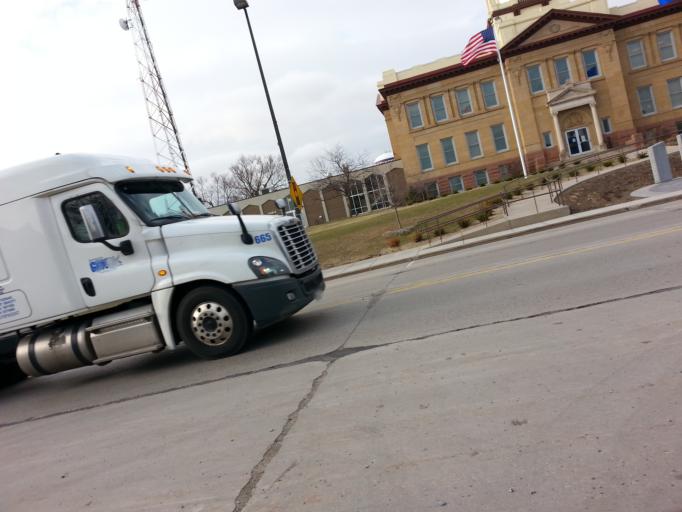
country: US
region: Wisconsin
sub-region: Pierce County
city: Ellsworth
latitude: 44.7320
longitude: -92.4851
